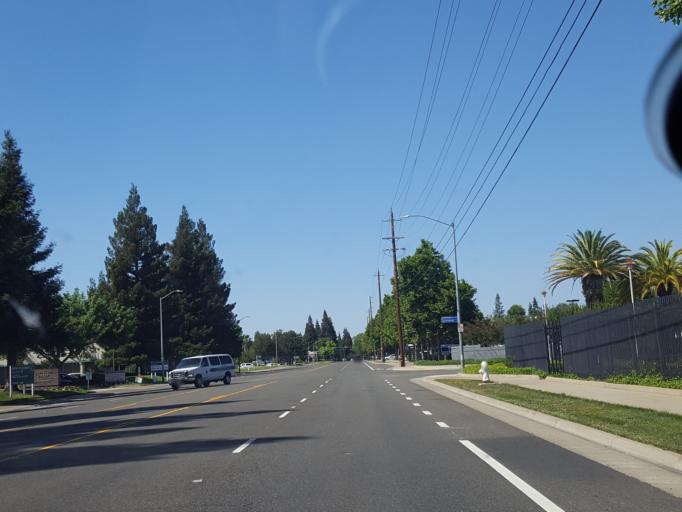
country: US
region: California
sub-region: Sacramento County
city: Rancho Cordova
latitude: 38.5699
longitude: -121.3067
